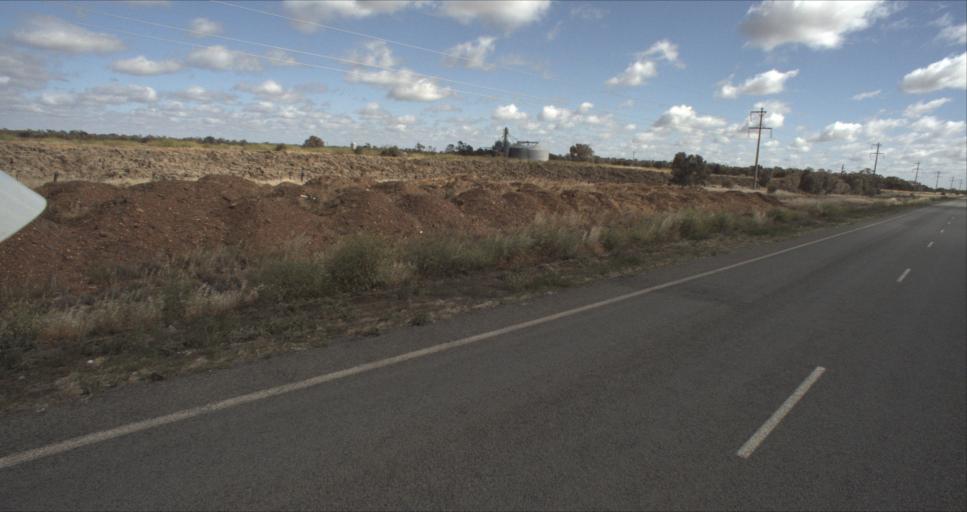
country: AU
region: New South Wales
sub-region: Murrumbidgee Shire
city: Darlington Point
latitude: -34.5510
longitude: 146.1706
